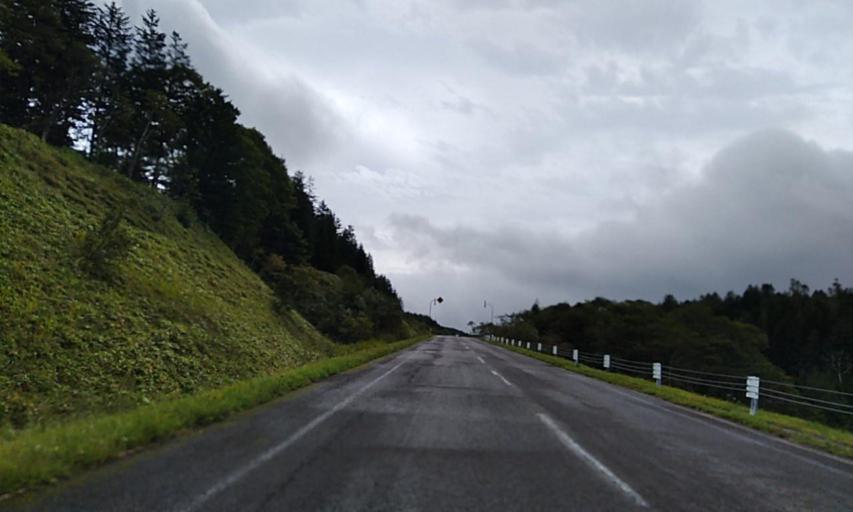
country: JP
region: Hokkaido
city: Abashiri
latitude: 43.6169
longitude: 144.5835
